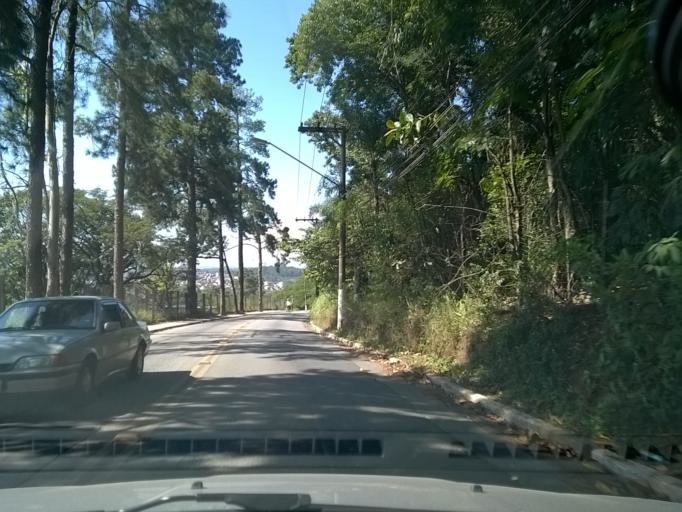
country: BR
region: Sao Paulo
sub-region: Caieiras
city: Caieiras
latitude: -23.3961
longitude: -46.7422
